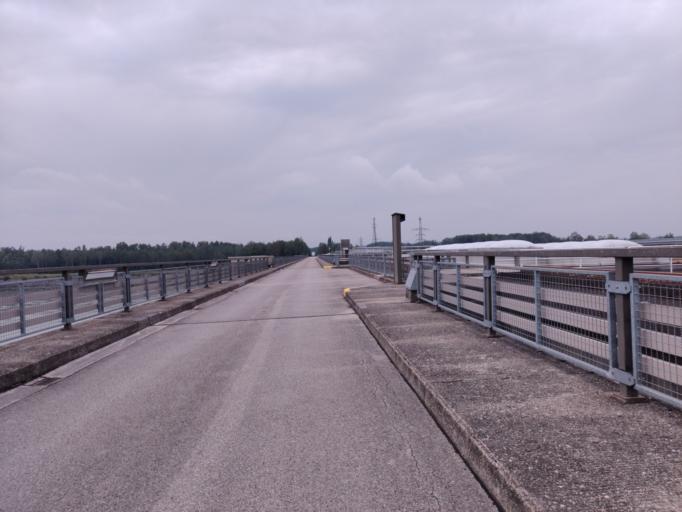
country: AT
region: Upper Austria
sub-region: Politischer Bezirk Linz-Land
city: Asten
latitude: 48.2499
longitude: 14.4324
